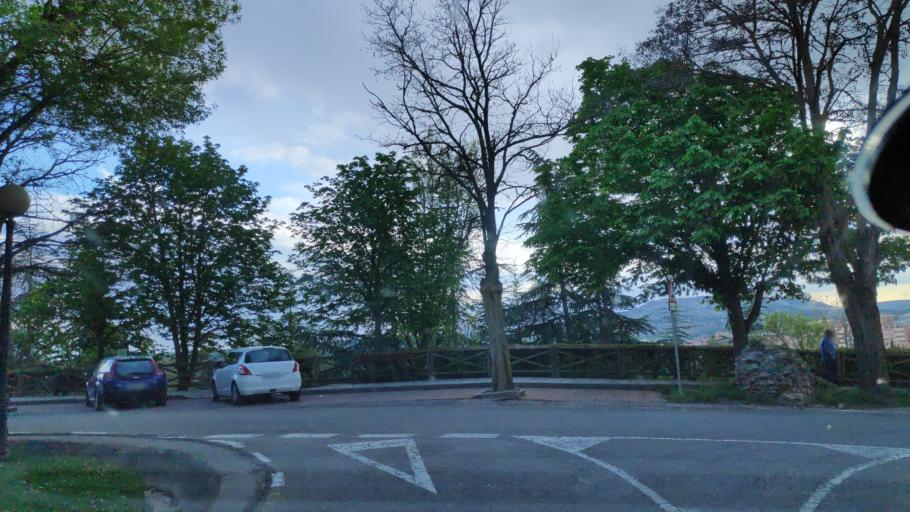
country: ES
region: Castille and Leon
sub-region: Provincia de Soria
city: Soria
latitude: 41.7616
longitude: -2.4595
